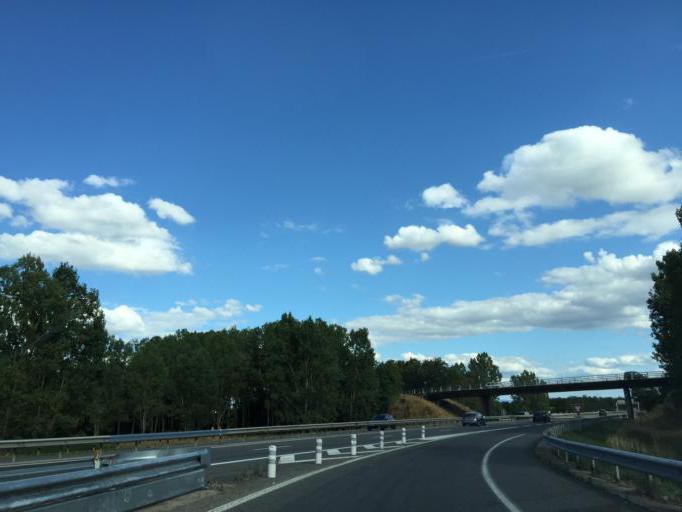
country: FR
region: Rhone-Alpes
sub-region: Departement de la Loire
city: Montrond-les-Bains
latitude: 45.6390
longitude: 4.1898
